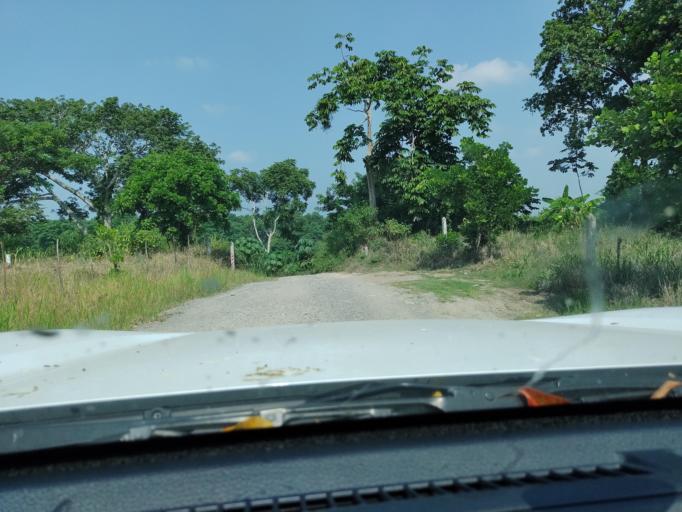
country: MX
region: Veracruz
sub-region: Martinez de la Torre
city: El Progreso
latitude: 20.0747
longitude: -97.0091
